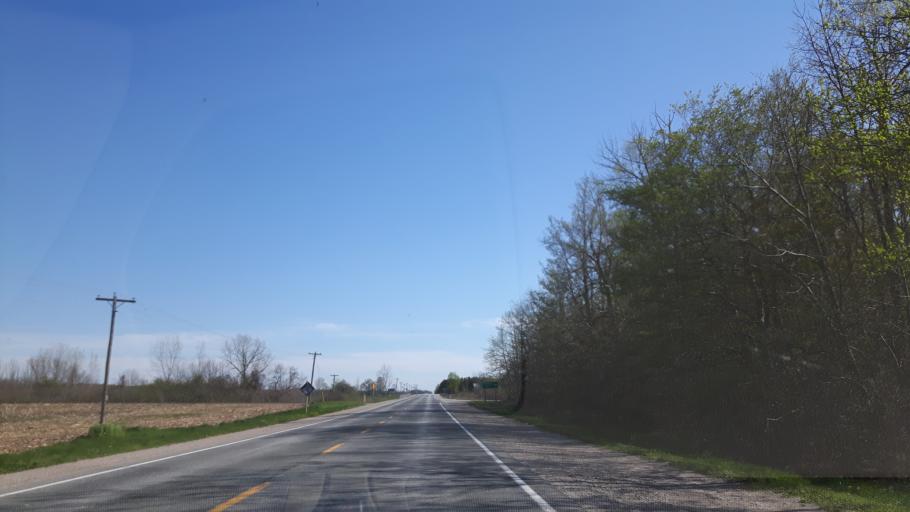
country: CA
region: Ontario
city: Bluewater
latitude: 43.5392
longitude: -81.6910
